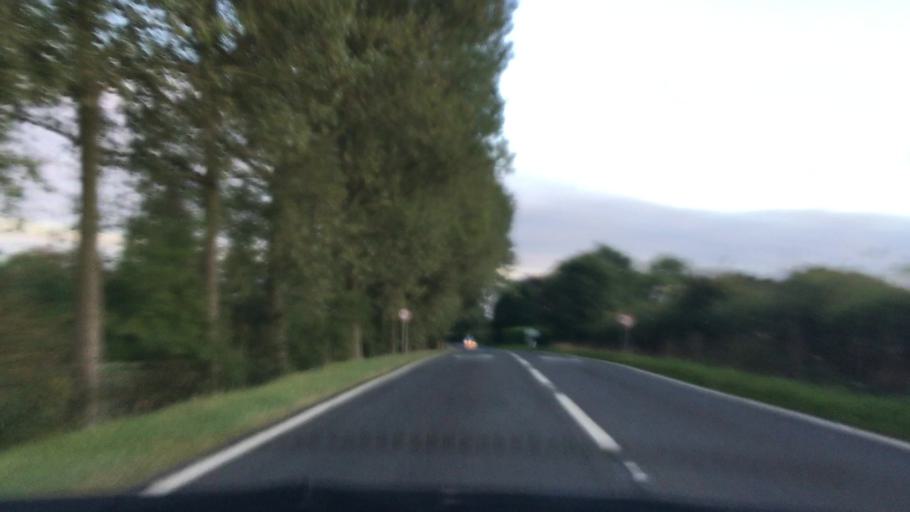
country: GB
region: England
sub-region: North East Lincolnshire
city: Wold Newton
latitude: 53.4664
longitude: -0.1041
